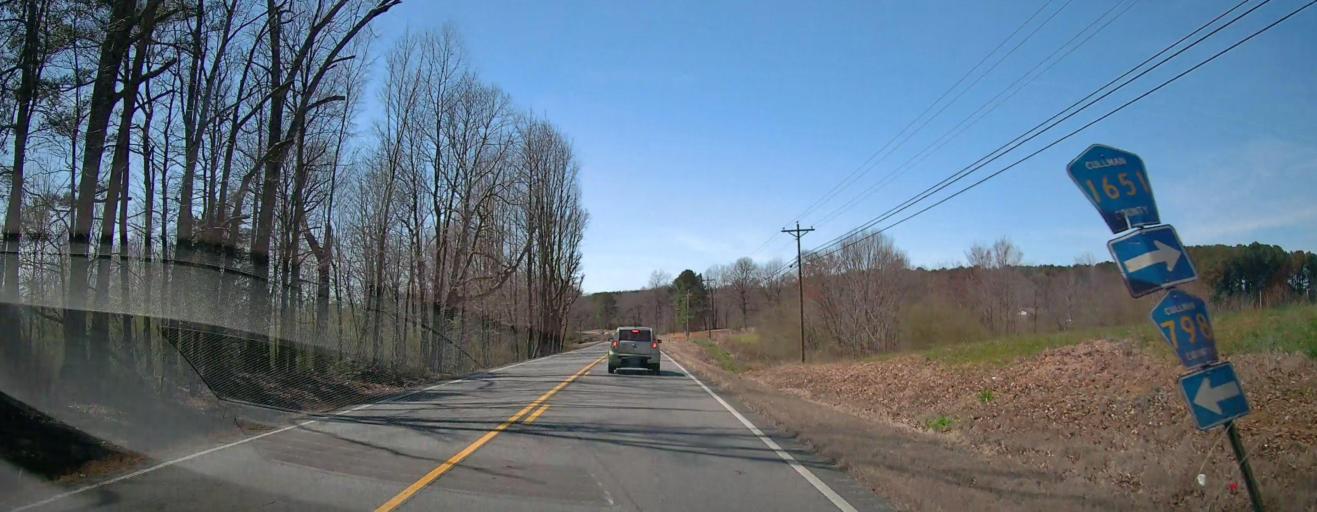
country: US
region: Alabama
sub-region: Blount County
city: Blountsville
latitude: 34.1752
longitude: -86.6708
